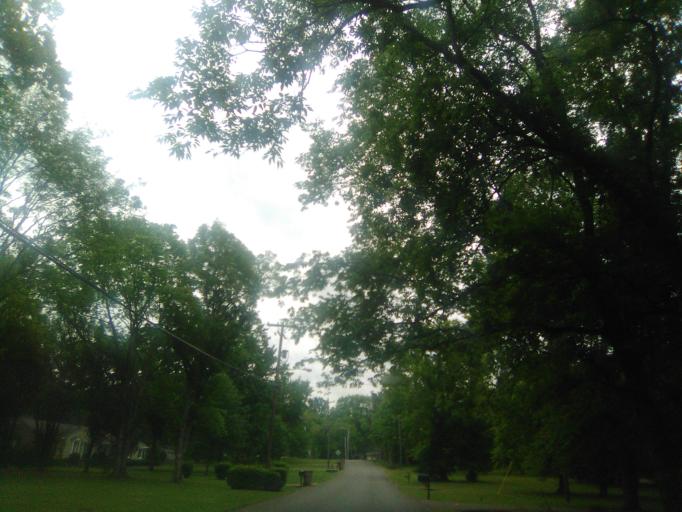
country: US
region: Tennessee
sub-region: Davidson County
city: Belle Meade
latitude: 36.1045
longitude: -86.8788
